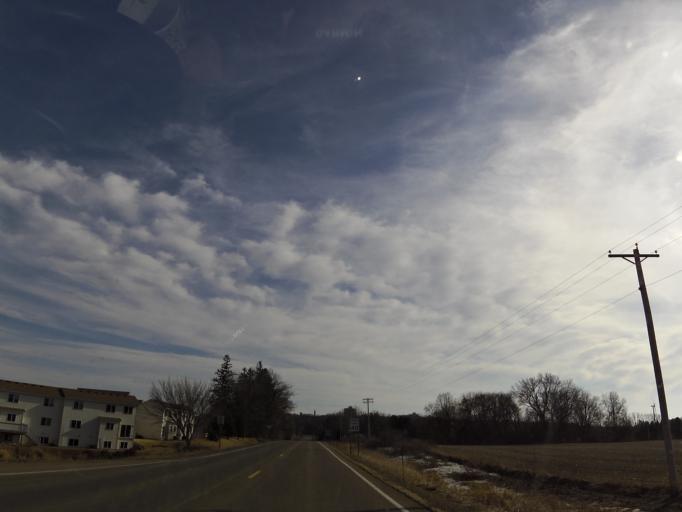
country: US
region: Minnesota
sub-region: Rice County
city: Northfield
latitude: 44.4735
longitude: -93.1808
